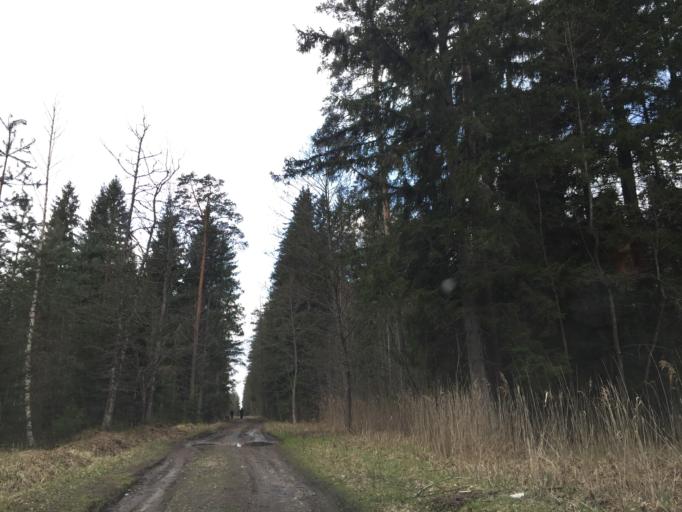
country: LV
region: Garkalne
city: Garkalne
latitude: 56.9639
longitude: 24.4840
